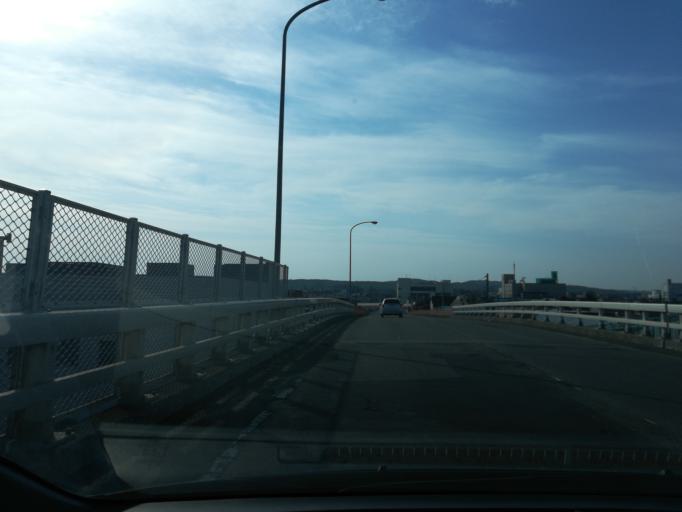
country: JP
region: Hokkaido
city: Iwamizawa
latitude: 43.2075
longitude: 141.7660
